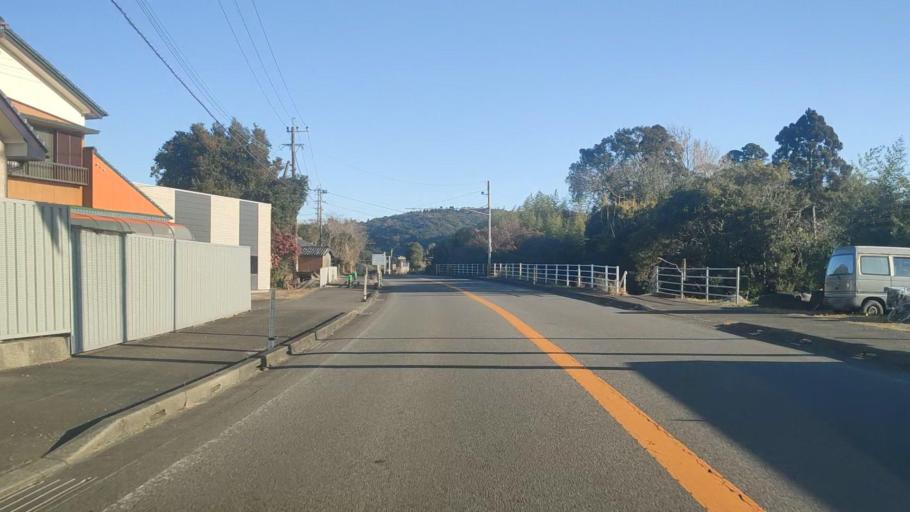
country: JP
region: Miyazaki
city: Takanabe
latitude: 32.3350
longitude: 131.6097
